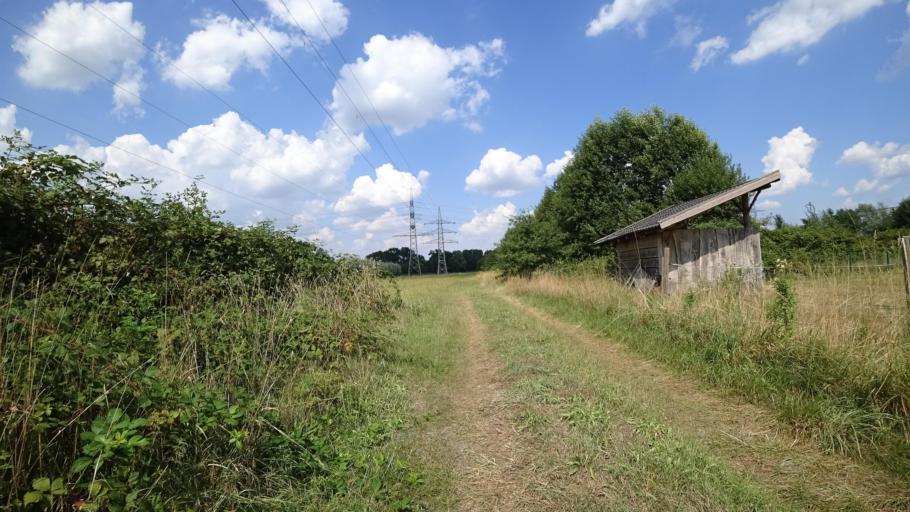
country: DE
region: North Rhine-Westphalia
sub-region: Regierungsbezirk Detmold
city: Guetersloh
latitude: 51.9259
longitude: 8.4210
